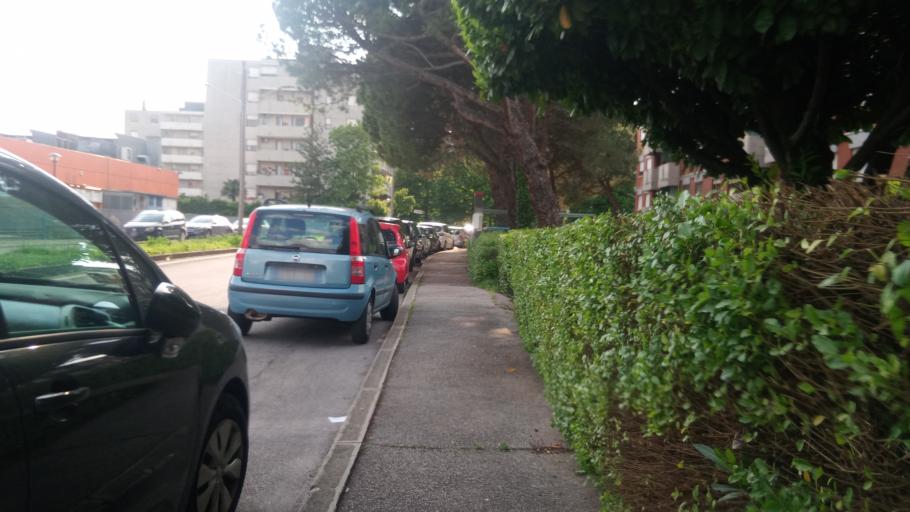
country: IT
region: Veneto
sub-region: Provincia di Padova
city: Cadoneghe
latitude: 45.4273
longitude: 11.9077
